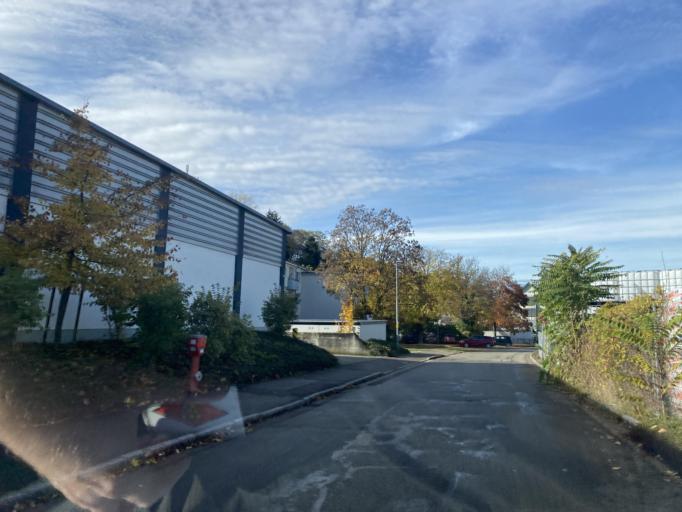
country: DE
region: Baden-Wuerttemberg
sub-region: Freiburg Region
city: Mullheim
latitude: 47.8051
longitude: 7.6254
